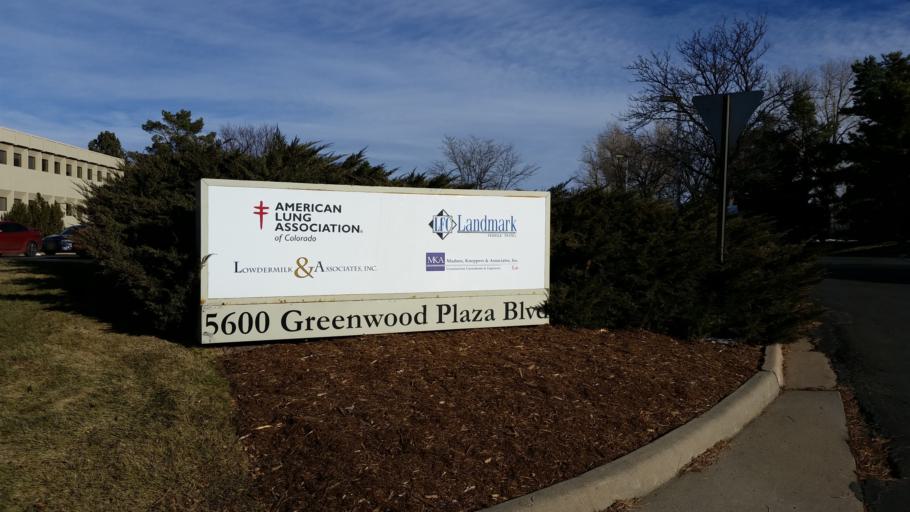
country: US
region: Colorado
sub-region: Arapahoe County
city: Castlewood
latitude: 39.6140
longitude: -104.8983
